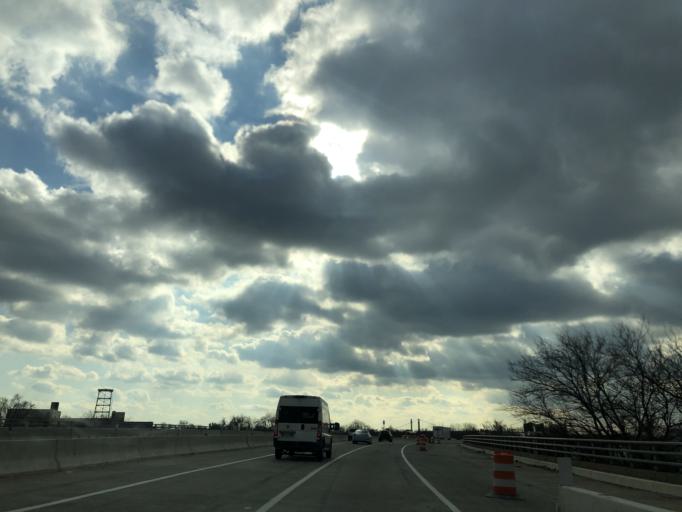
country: US
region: New Jersey
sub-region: Camden County
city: Camden
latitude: 39.9336
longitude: -75.1116
